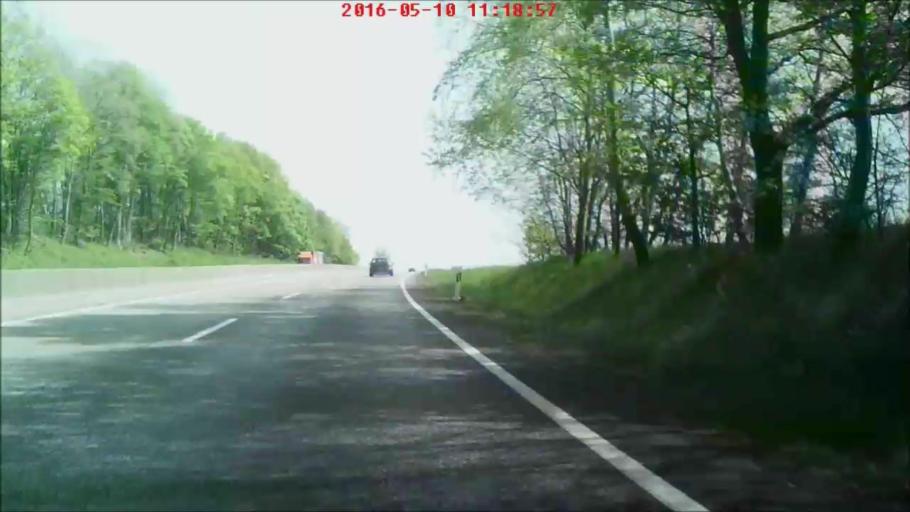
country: DE
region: Thuringia
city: Grossensee
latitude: 50.9508
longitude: 9.9729
